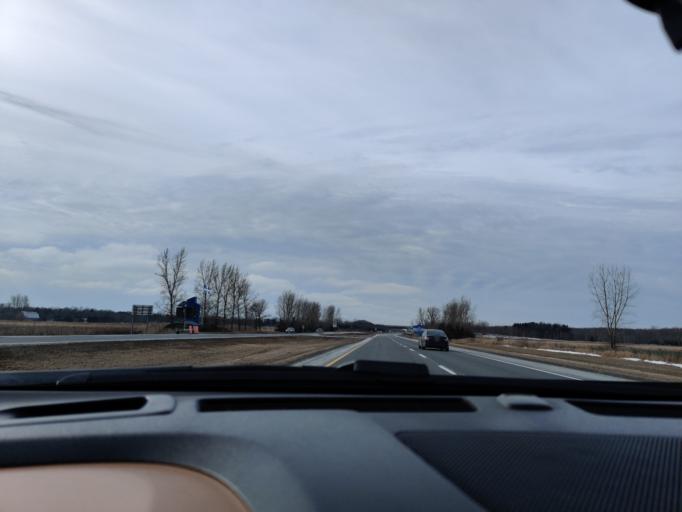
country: CA
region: Quebec
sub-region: Monteregie
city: Les Coteaux
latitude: 45.2101
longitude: -74.3461
